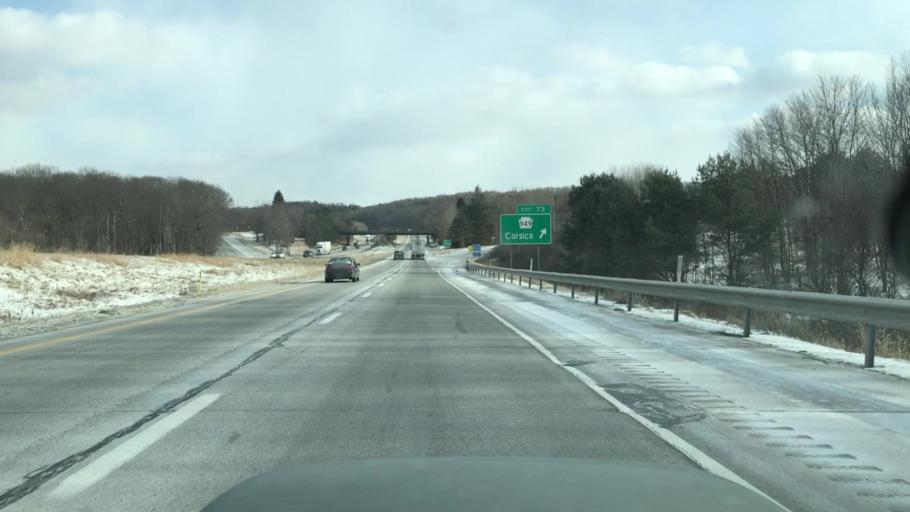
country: US
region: Pennsylvania
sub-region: Jefferson County
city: Brookville
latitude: 41.1876
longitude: -79.2026
